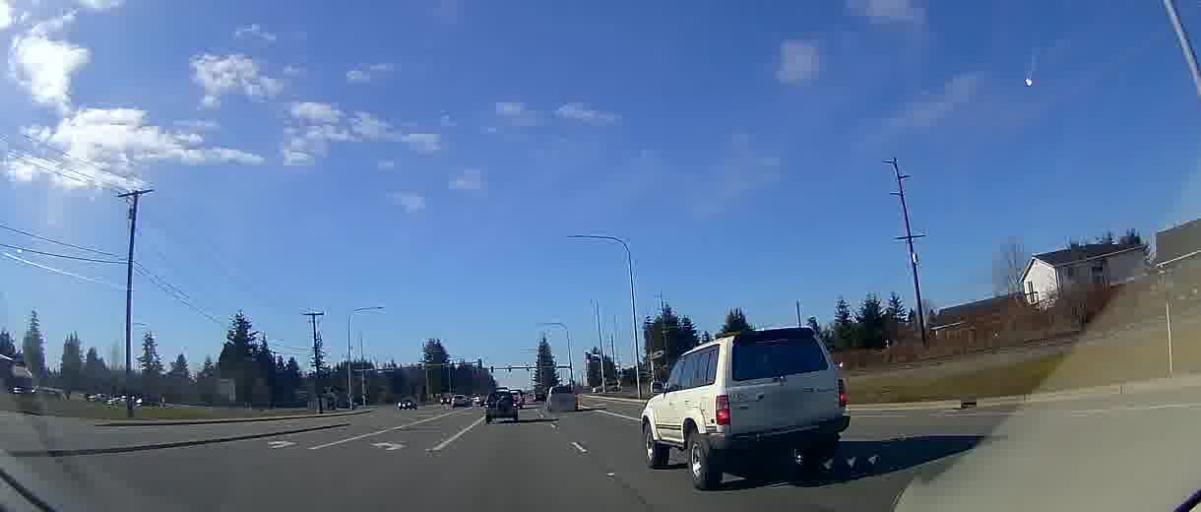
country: US
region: Washington
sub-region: Skagit County
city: Burlington
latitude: 48.4695
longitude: -122.3459
